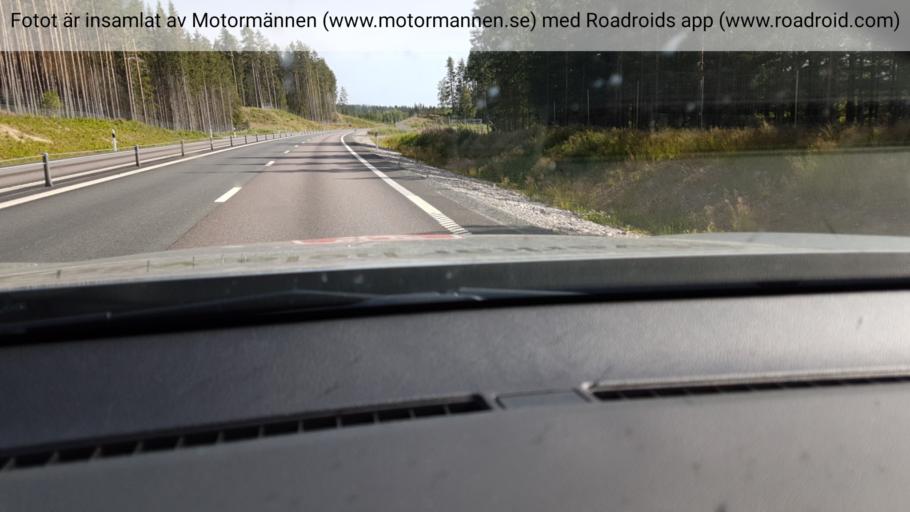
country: SE
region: Joenkoeping
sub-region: Aneby Kommun
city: Aneby
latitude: 57.8372
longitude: 14.8739
